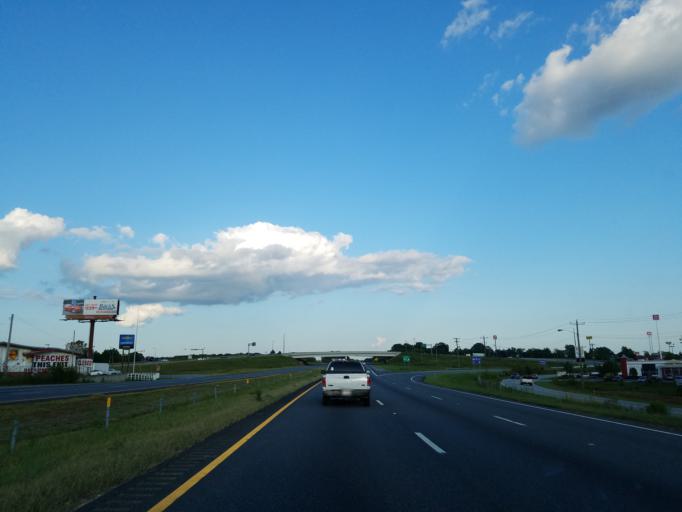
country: US
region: South Carolina
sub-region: Cherokee County
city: Gaffney
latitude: 35.0973
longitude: -81.6727
